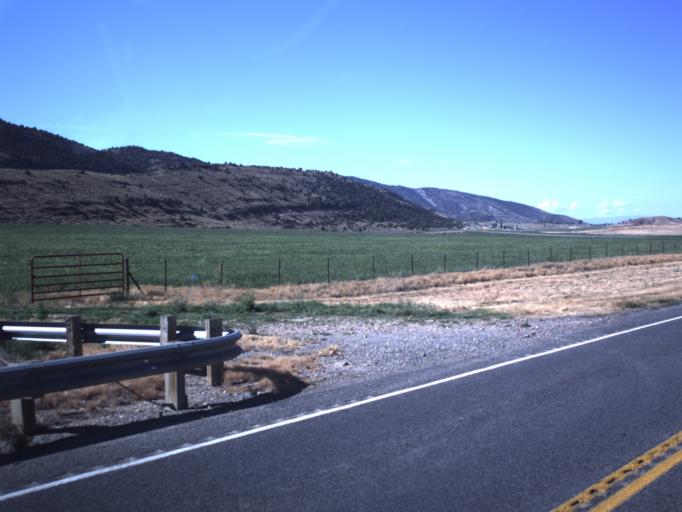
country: US
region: Utah
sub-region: Sanpete County
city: Manti
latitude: 39.2287
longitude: -111.6700
